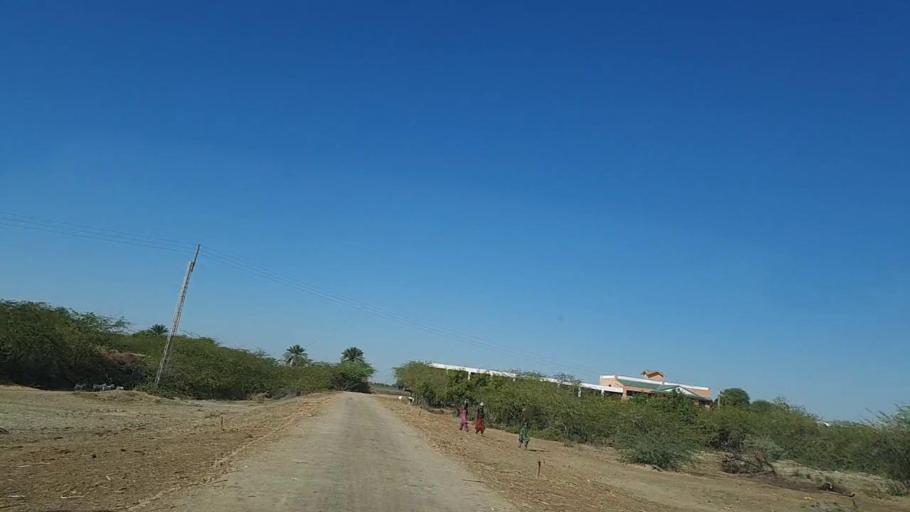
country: PK
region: Sindh
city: Dhoro Naro
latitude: 25.5359
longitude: 69.4808
